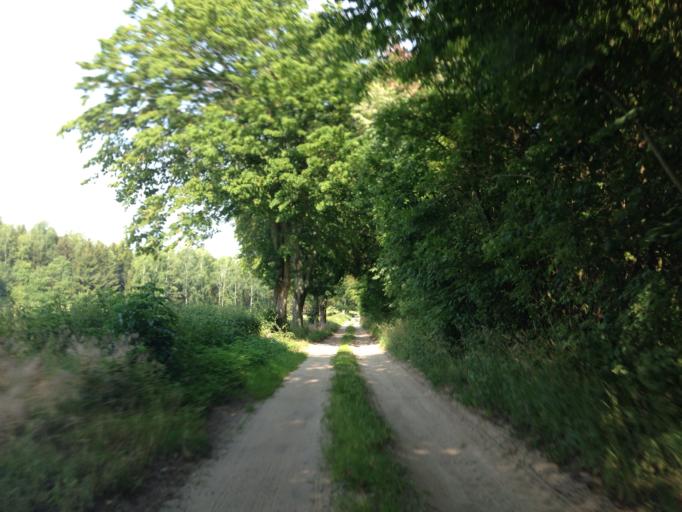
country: PL
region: Kujawsko-Pomorskie
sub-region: Powiat rypinski
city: Wapielsk
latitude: 53.2027
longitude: 19.2550
